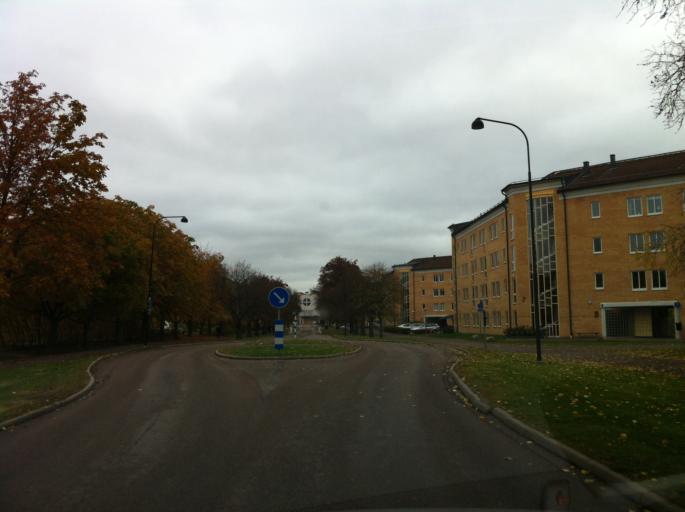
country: SE
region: OEstergoetland
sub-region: Linkopings Kommun
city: Linkoping
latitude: 58.4015
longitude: 15.6047
